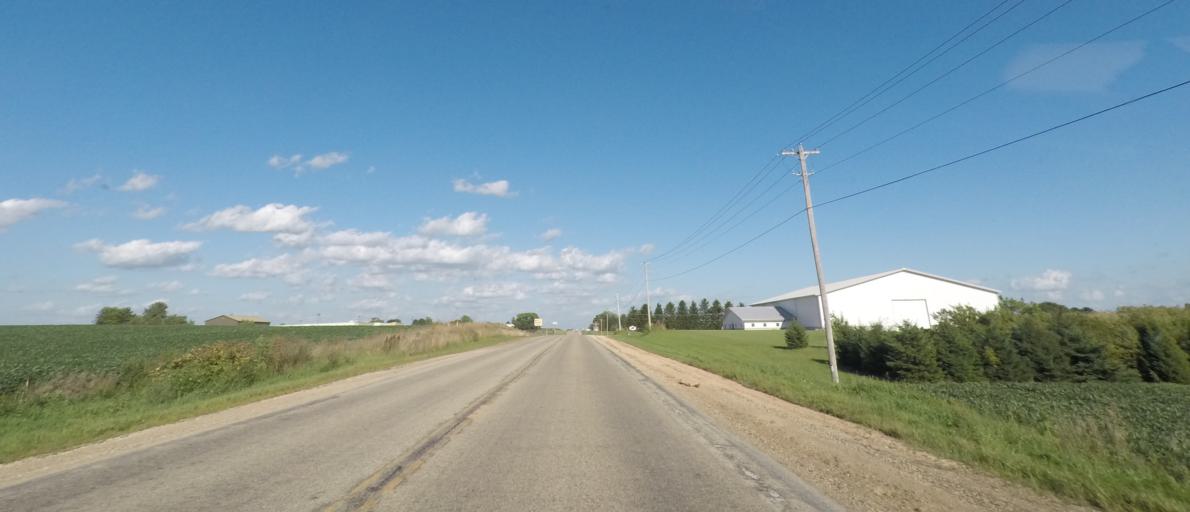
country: US
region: Wisconsin
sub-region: Iowa County
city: Dodgeville
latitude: 42.9817
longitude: -90.1108
